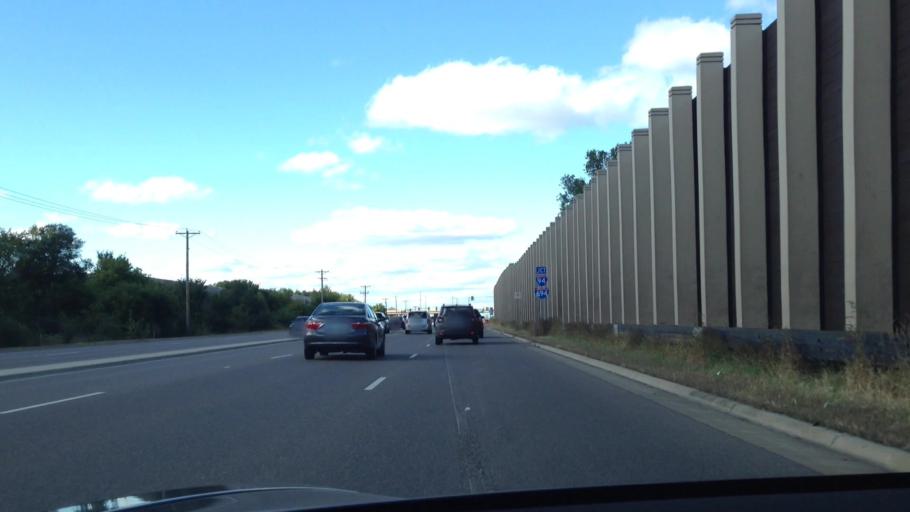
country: US
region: Minnesota
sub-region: Hennepin County
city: Brooklyn Park
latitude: 45.0730
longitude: -93.3702
